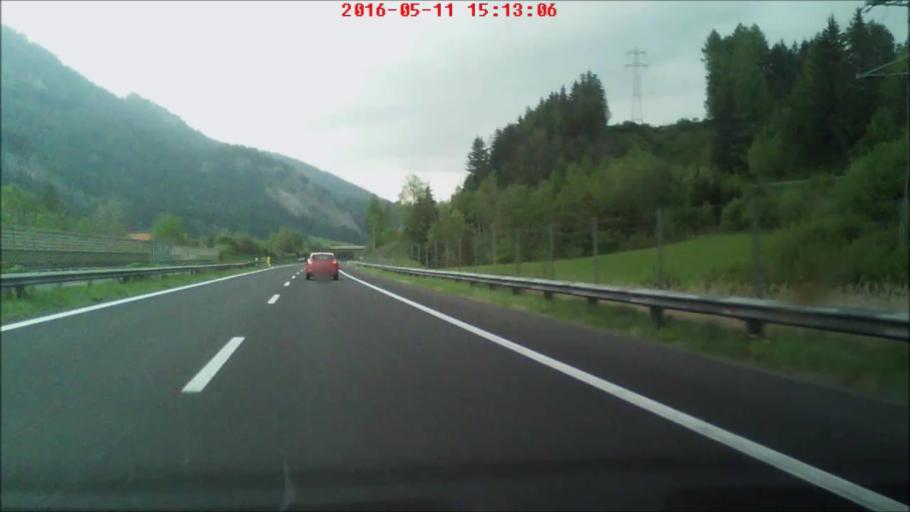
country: AT
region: Styria
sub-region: Politischer Bezirk Leoben
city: Mautern in Steiermark
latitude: 47.3949
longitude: 14.8408
